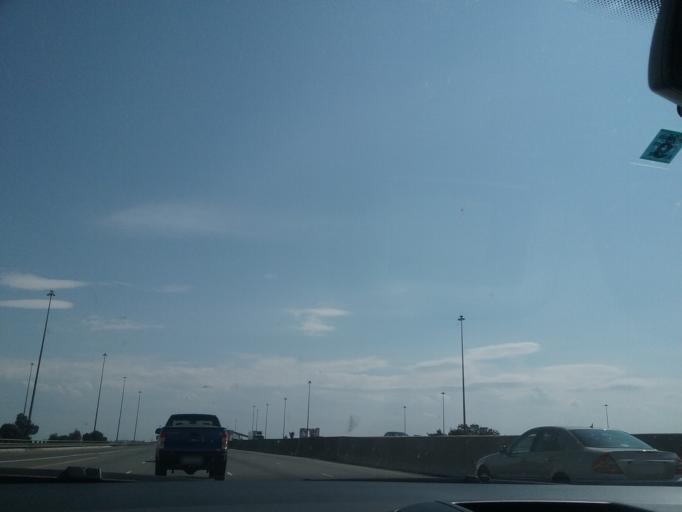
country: ZA
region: Gauteng
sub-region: Ekurhuleni Metropolitan Municipality
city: Germiston
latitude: -26.2117
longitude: 28.1351
